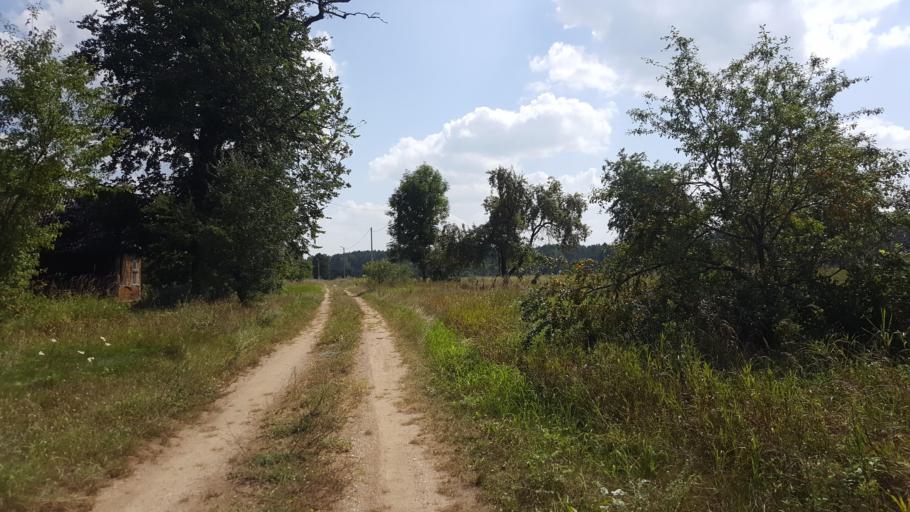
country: PL
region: Podlasie
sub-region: Powiat hajnowski
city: Hajnowka
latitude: 52.5749
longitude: 23.5480
